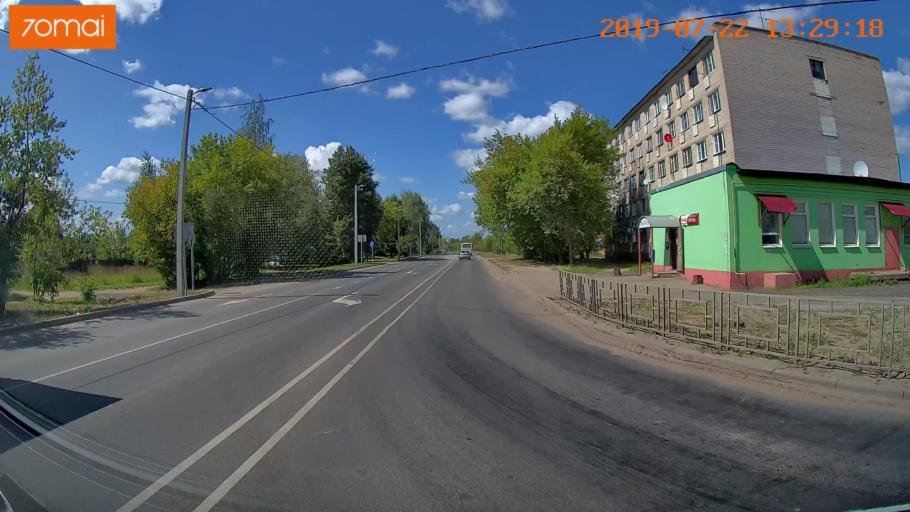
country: RU
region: Ivanovo
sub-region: Gorod Ivanovo
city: Ivanovo
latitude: 57.0465
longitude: 40.9404
